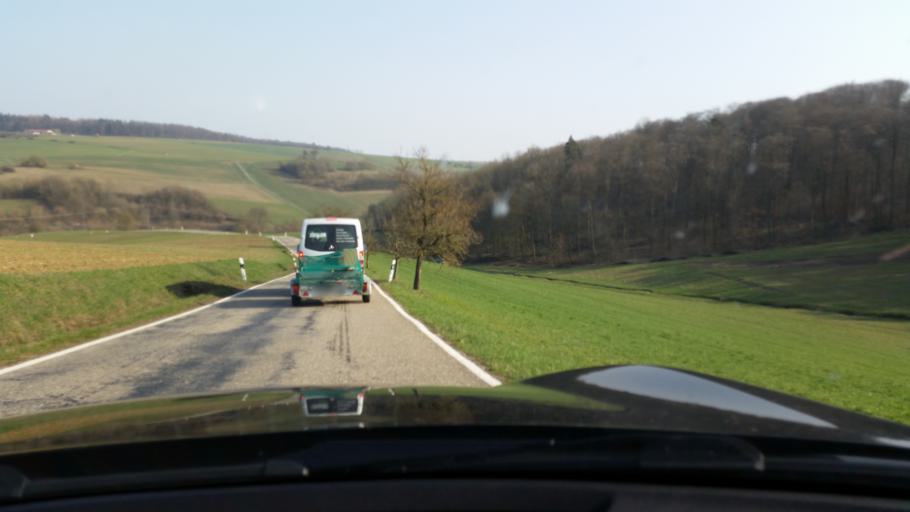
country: DE
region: Baden-Wuerttemberg
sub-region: Regierungsbezirk Stuttgart
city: Mockmuhl
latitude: 49.3497
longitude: 9.3826
